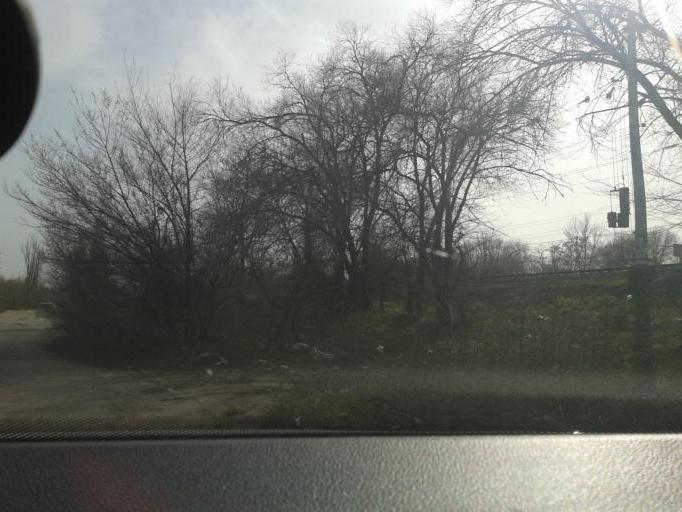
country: RU
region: Volgograd
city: Volgograd
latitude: 48.6348
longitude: 44.4386
